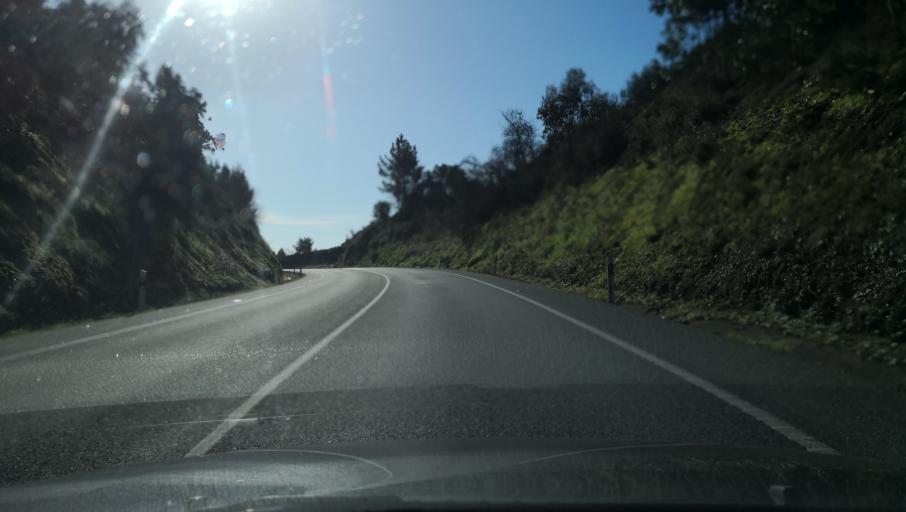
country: ES
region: Galicia
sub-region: Provincia da Coruna
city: Vedra
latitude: 42.7893
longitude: -8.4429
